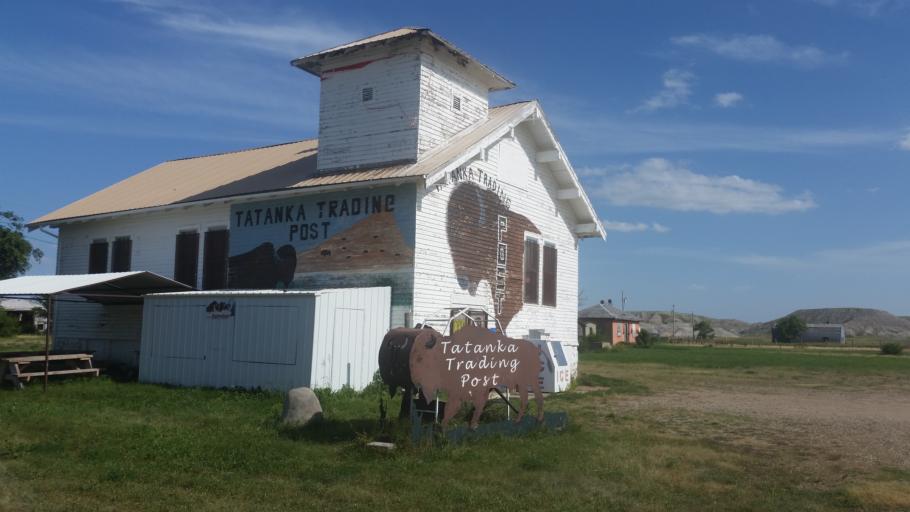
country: US
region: South Dakota
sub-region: Shannon County
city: Porcupine
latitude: 43.7797
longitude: -102.5522
